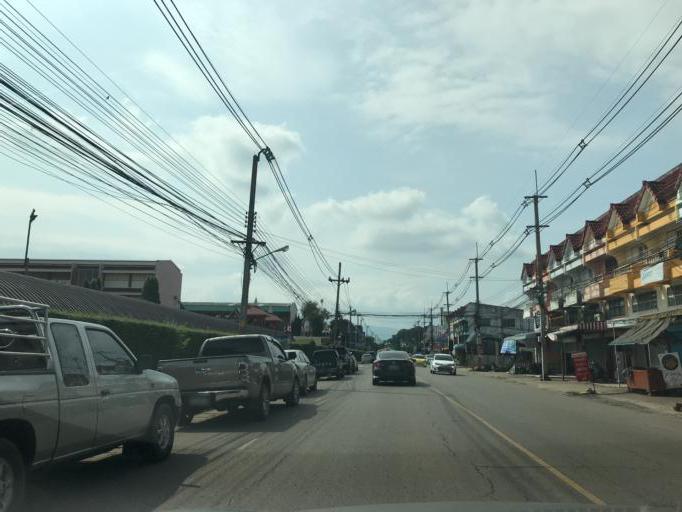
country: TH
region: Phayao
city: Chiang Kham
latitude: 19.5189
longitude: 100.3105
